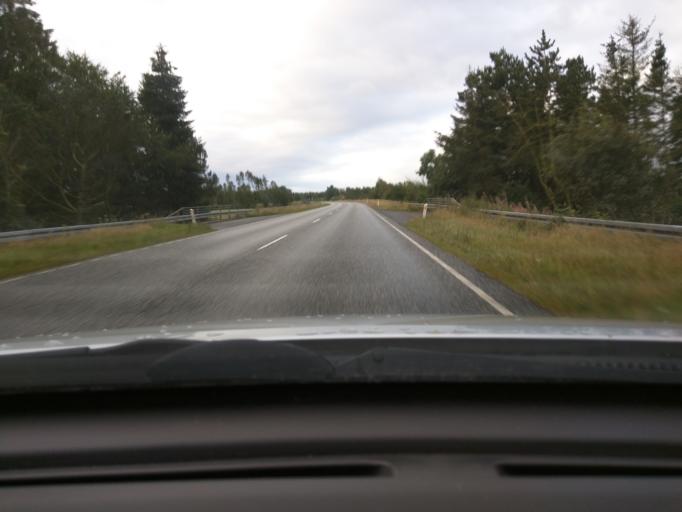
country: DK
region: Central Jutland
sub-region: Ikast-Brande Kommune
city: Bording Kirkeby
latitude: 56.1956
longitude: 9.3159
